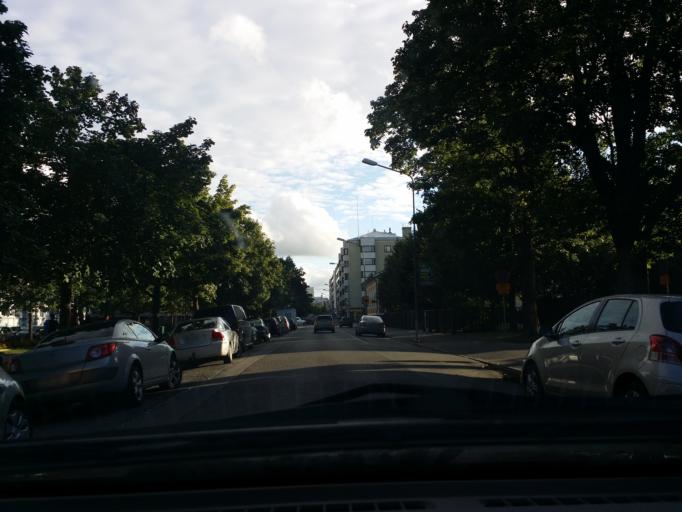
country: FI
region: Satakunta
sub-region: Pori
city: Pori
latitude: 61.4870
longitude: 21.7922
